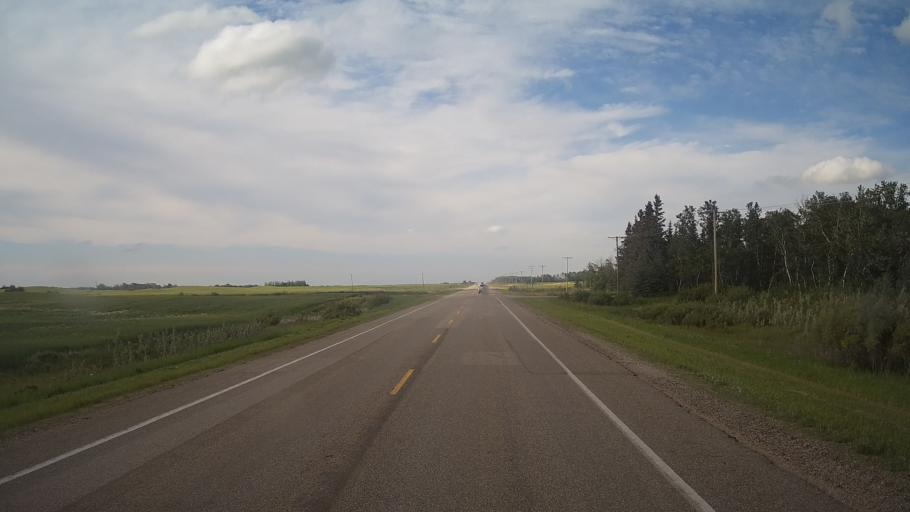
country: CA
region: Saskatchewan
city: Foam Lake
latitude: 51.6052
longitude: -103.8459
